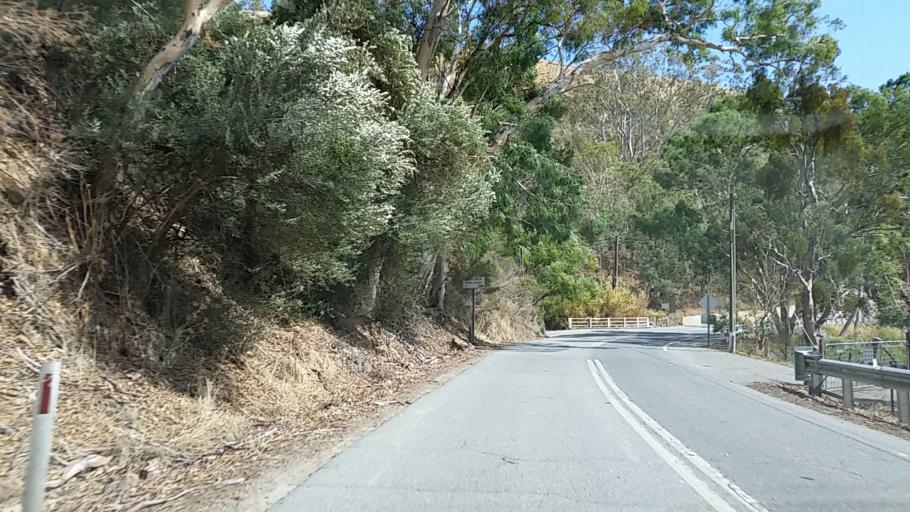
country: AU
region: South Australia
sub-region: Campbelltown
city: Athelstone
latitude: -34.8696
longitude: 138.7536
